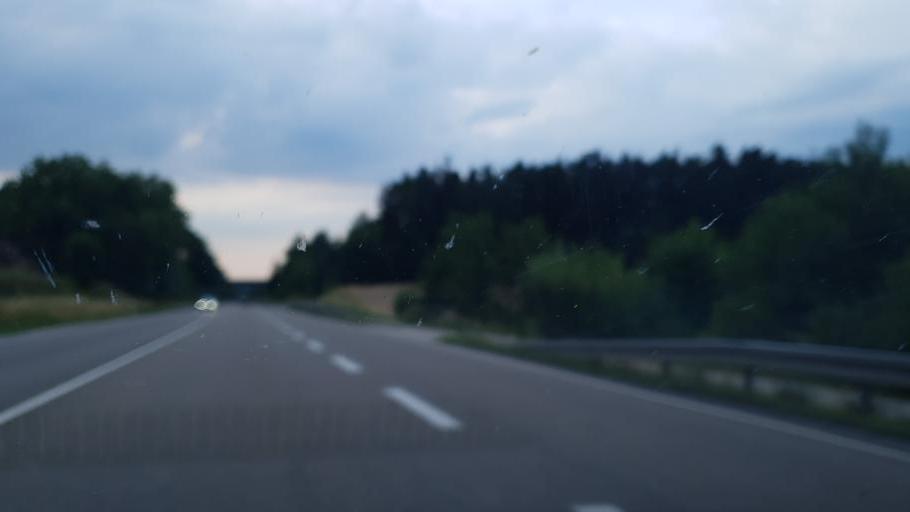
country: DE
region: Bavaria
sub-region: Regierungsbezirk Mittelfranken
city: Burgoberbach
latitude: 49.2610
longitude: 10.5880
